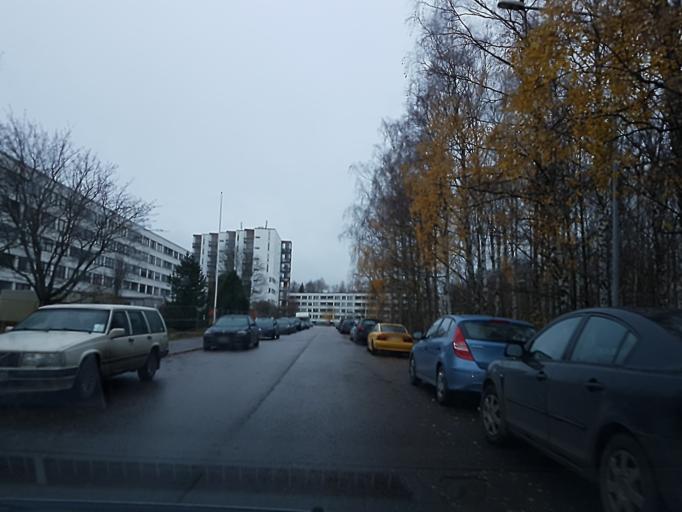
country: FI
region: Uusimaa
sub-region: Helsinki
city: Vantaa
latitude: 60.2312
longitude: 25.0869
